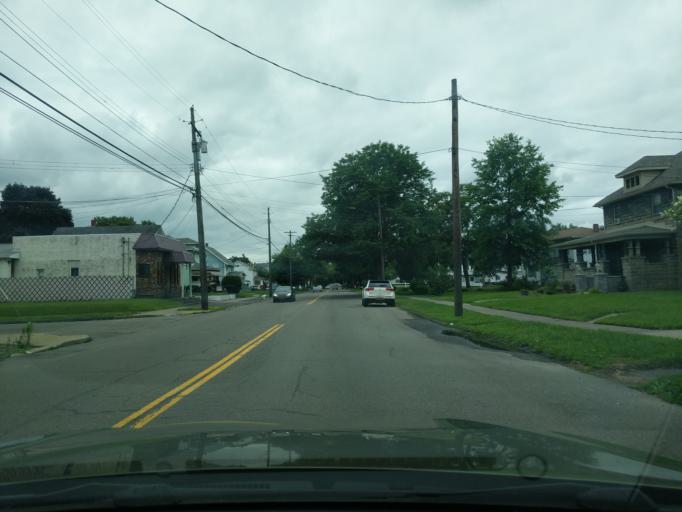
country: US
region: New York
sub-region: Chemung County
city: Elmira Heights
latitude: 42.1082
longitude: -76.8195
